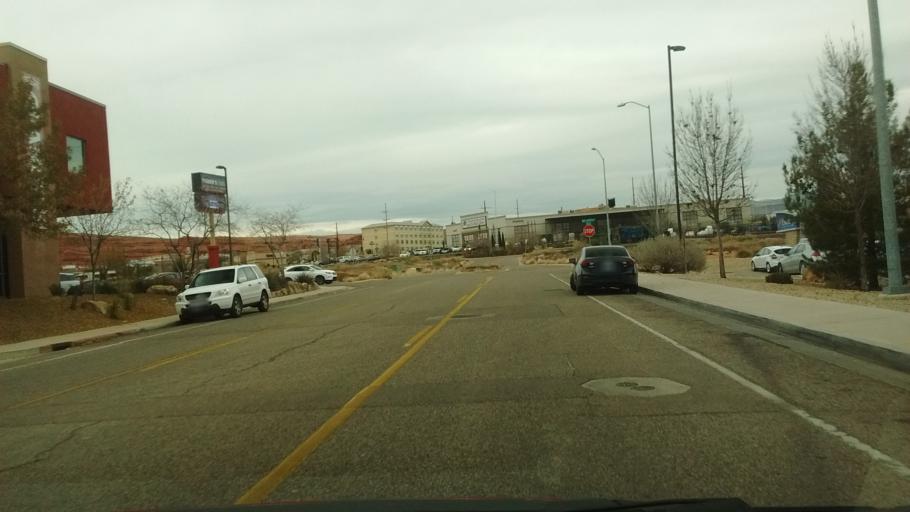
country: US
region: Utah
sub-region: Washington County
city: Washington
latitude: 37.1223
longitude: -113.5253
